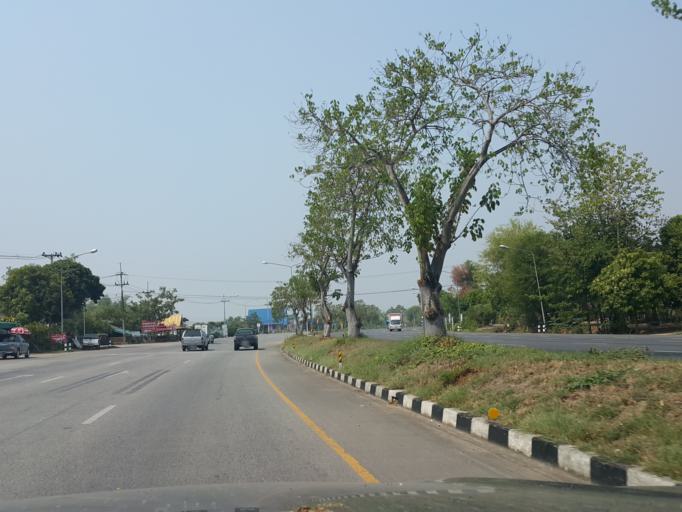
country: TH
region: Lampang
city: Thoen
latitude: 17.6536
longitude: 99.2509
